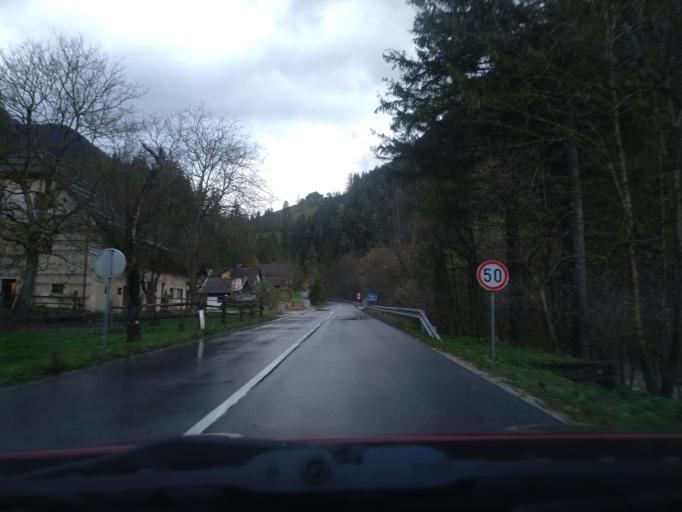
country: SI
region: Solcava
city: Solcava
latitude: 46.3951
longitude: 14.7124
